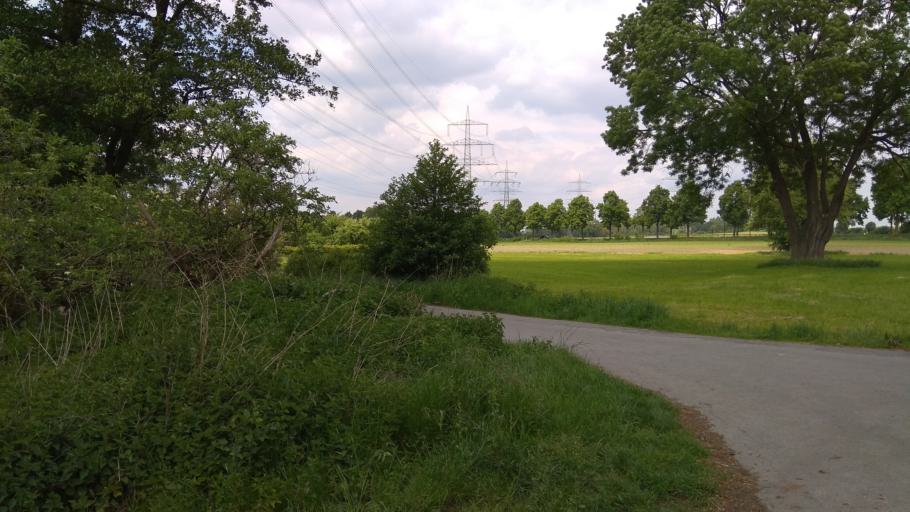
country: DE
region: North Rhine-Westphalia
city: Herten
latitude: 51.5930
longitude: 7.1138
